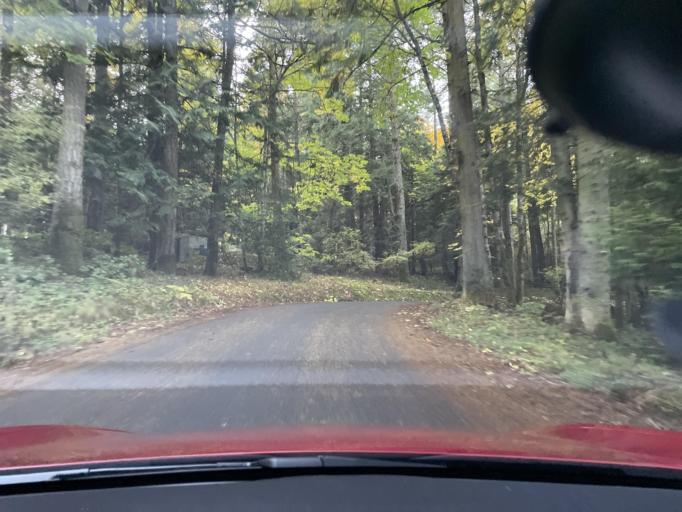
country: US
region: Washington
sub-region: San Juan County
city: Friday Harbor
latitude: 48.6013
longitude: -123.1521
